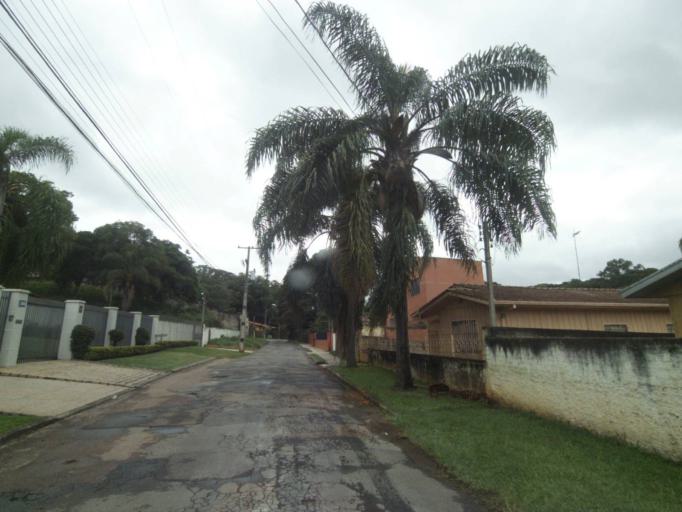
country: BR
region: Parana
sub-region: Curitiba
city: Curitiba
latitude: -25.4487
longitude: -49.3243
